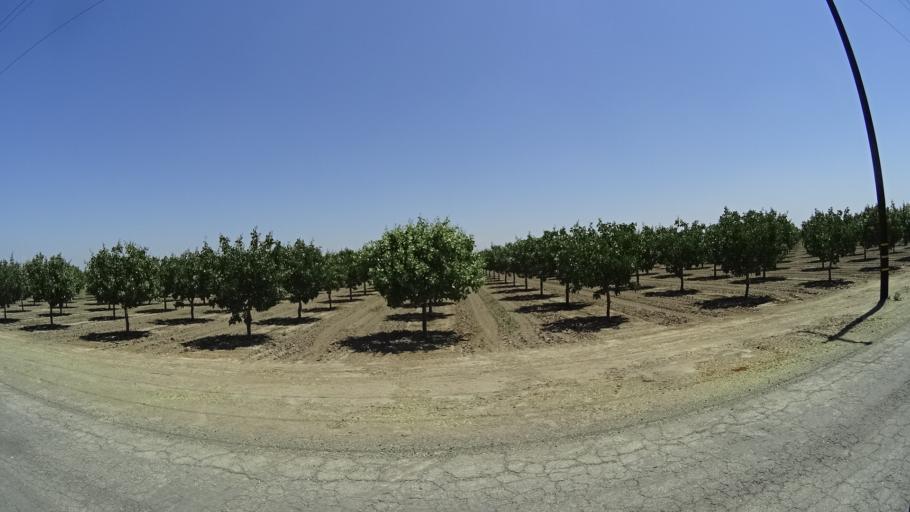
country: US
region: California
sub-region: Fresno County
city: Laton
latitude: 36.3966
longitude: -119.7270
